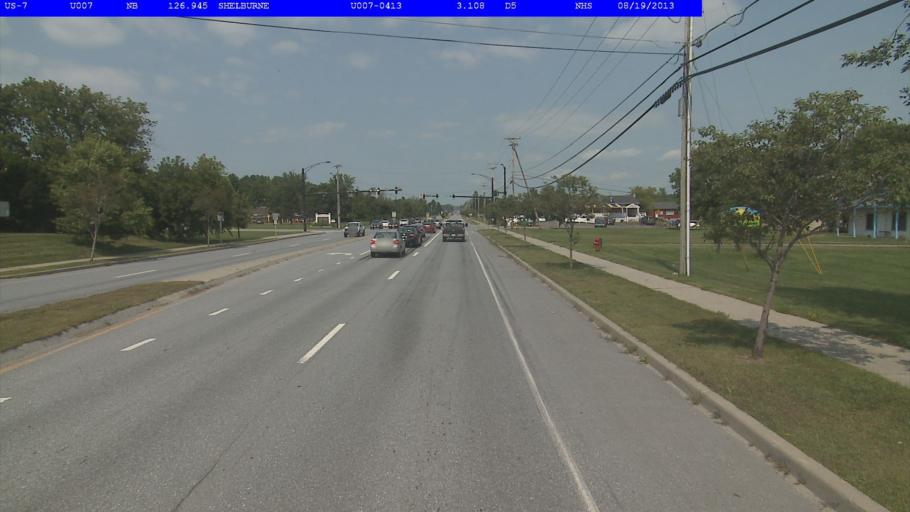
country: US
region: Vermont
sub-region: Chittenden County
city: Burlington
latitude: 44.3952
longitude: -73.2200
